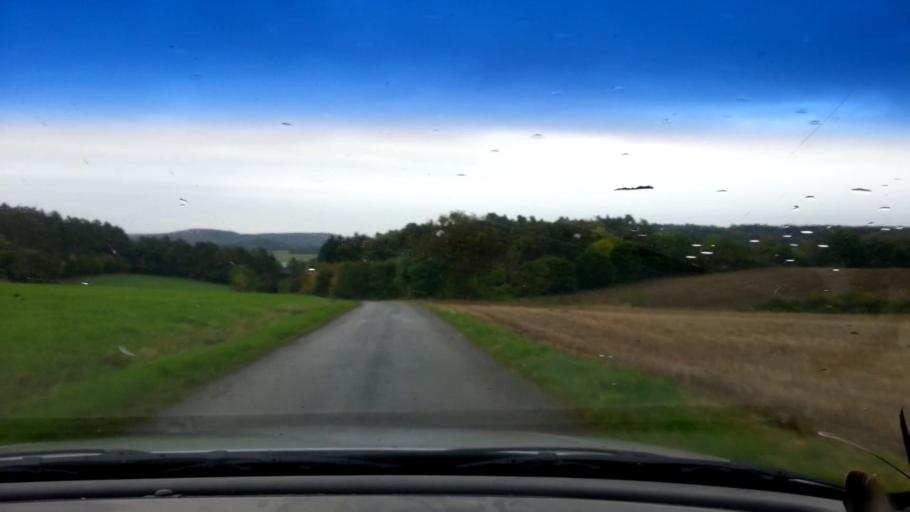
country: DE
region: Bavaria
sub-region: Upper Franconia
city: Poxdorf
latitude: 49.8916
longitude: 11.0898
